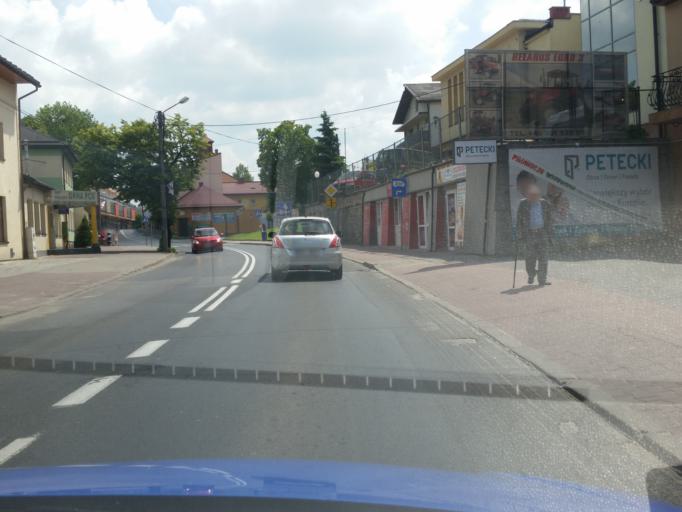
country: PL
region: Lesser Poland Voivodeship
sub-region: Powiat miechowski
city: Miechow
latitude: 50.3563
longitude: 20.0237
